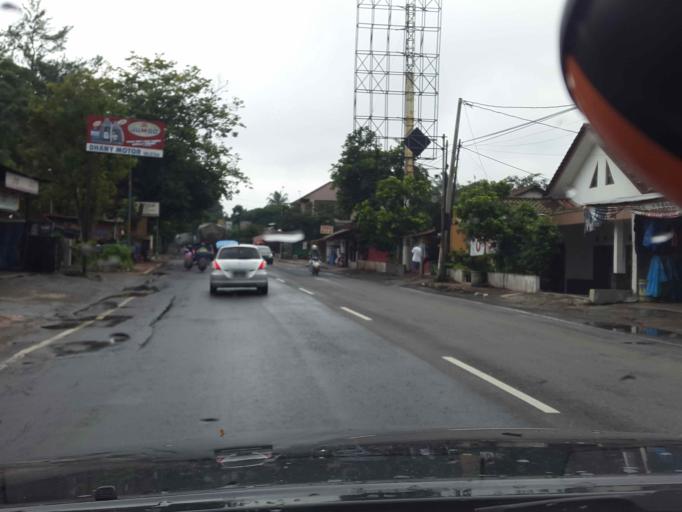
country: ID
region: Central Java
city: Salatiga
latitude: -7.3123
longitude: 110.4916
